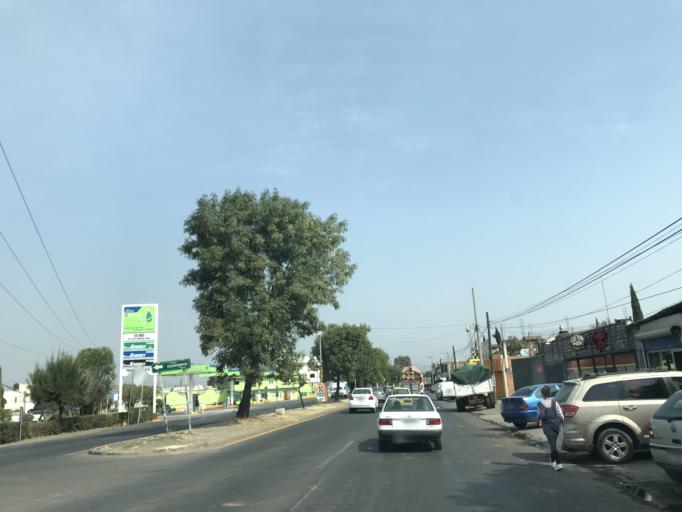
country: MX
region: Tlaxcala
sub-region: Teolocholco
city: Teolocholco
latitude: 19.2532
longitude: -98.1979
